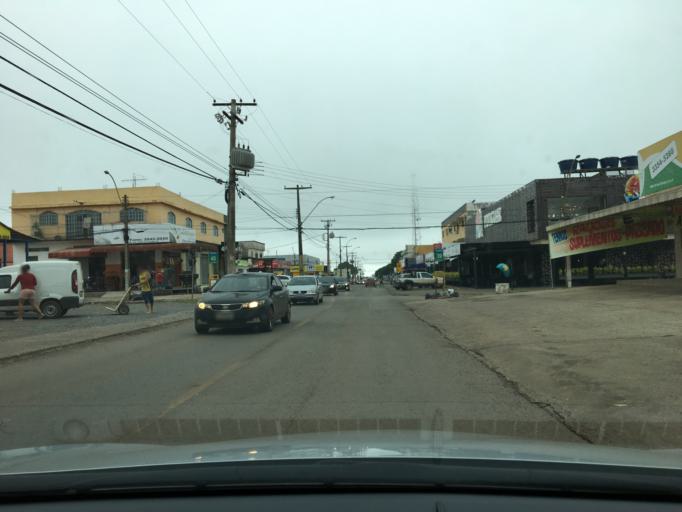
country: BR
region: Federal District
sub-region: Brasilia
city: Brasilia
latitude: -15.8065
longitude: -48.0616
